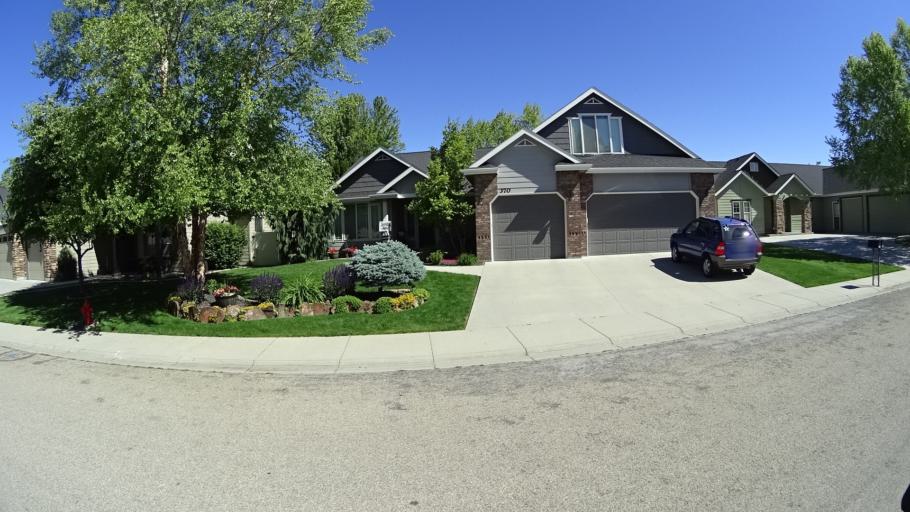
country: US
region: Idaho
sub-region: Ada County
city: Meridian
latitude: 43.6425
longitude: -116.3894
